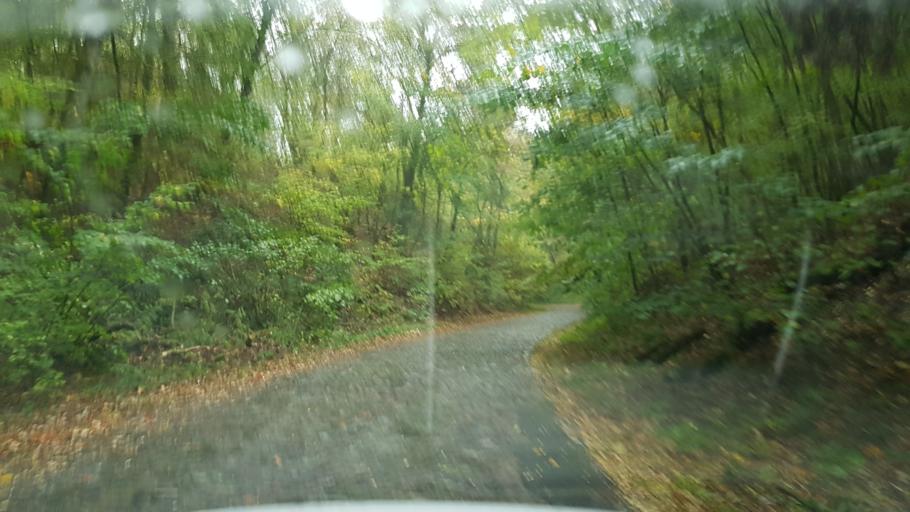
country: PL
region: West Pomeranian Voivodeship
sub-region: Powiat mysliborski
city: Barlinek
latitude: 53.0328
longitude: 15.2351
